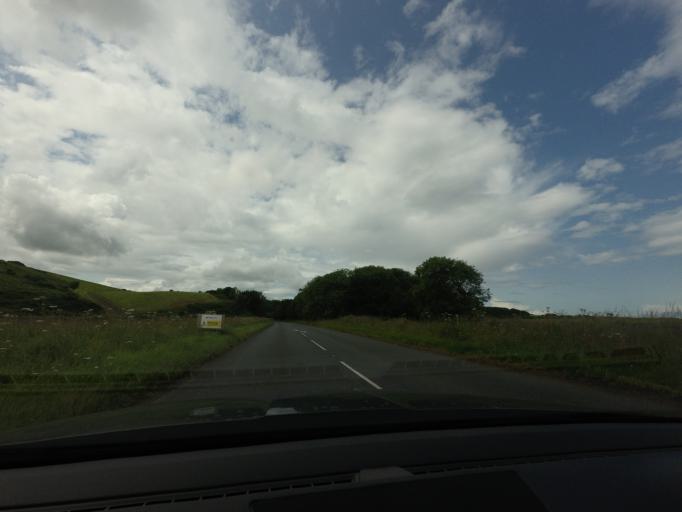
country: GB
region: Scotland
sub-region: Aberdeenshire
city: Whitehills
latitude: 57.6648
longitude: -2.5693
